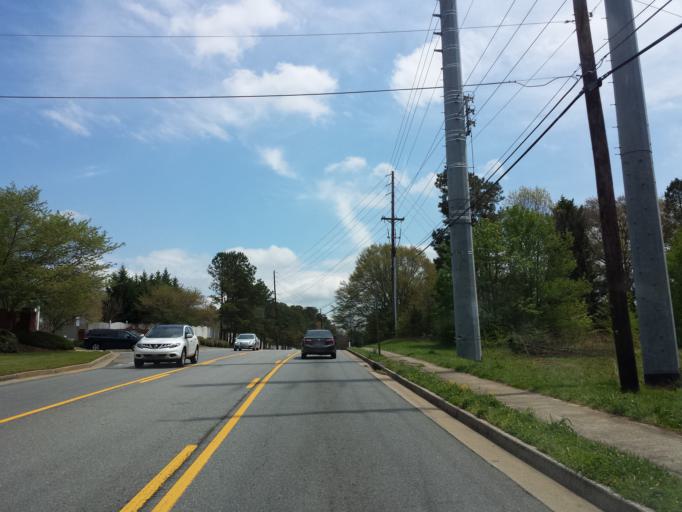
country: US
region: Georgia
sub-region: Cobb County
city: Marietta
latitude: 34.0126
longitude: -84.4795
